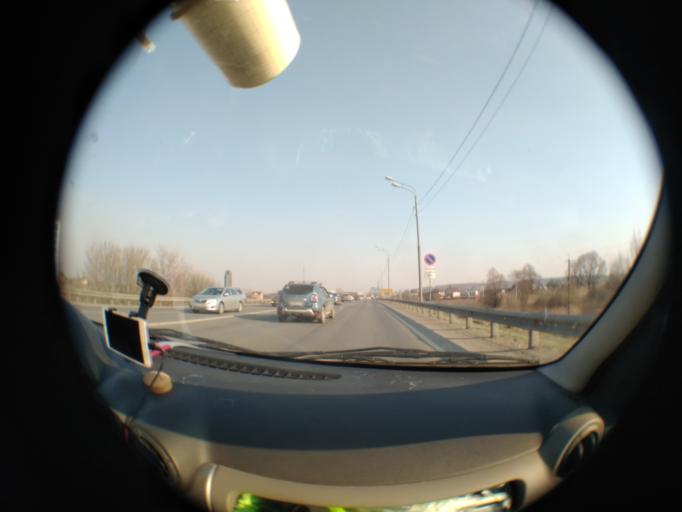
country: RU
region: Moskovskaya
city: Ostrovtsy
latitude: 55.5752
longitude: 38.0255
